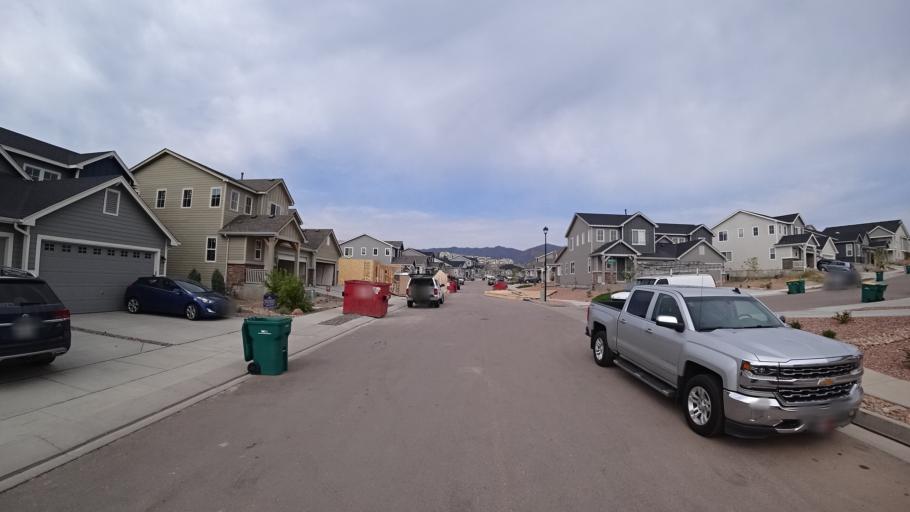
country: US
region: Colorado
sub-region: El Paso County
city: Colorado Springs
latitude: 38.9160
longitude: -104.8243
